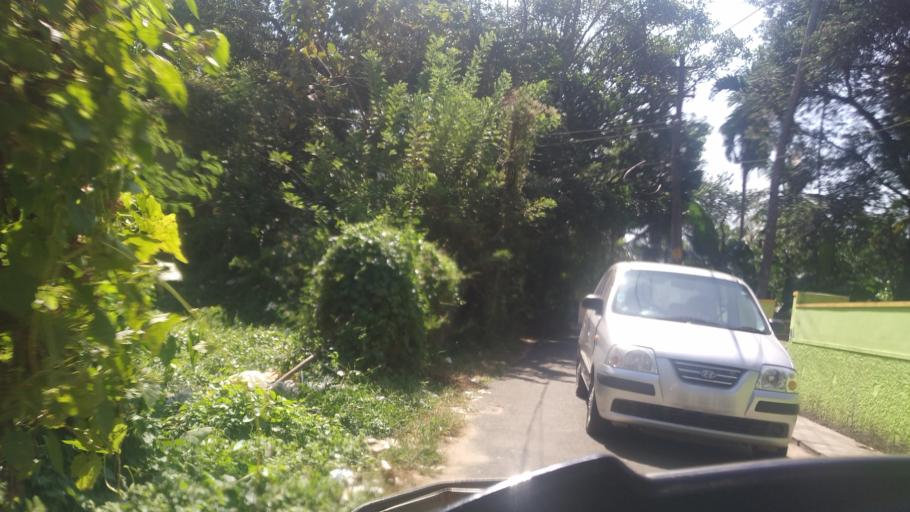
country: IN
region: Kerala
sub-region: Ernakulam
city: Elur
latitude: 10.0342
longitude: 76.2254
